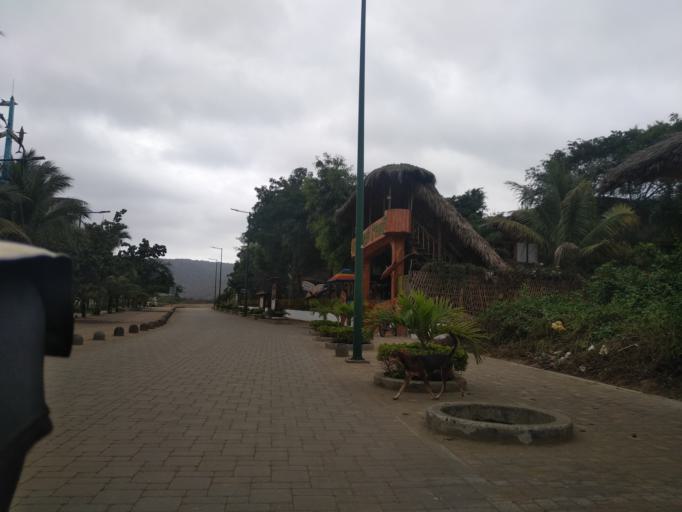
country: EC
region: Manabi
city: Jipijapa
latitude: -1.5500
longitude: -80.8107
